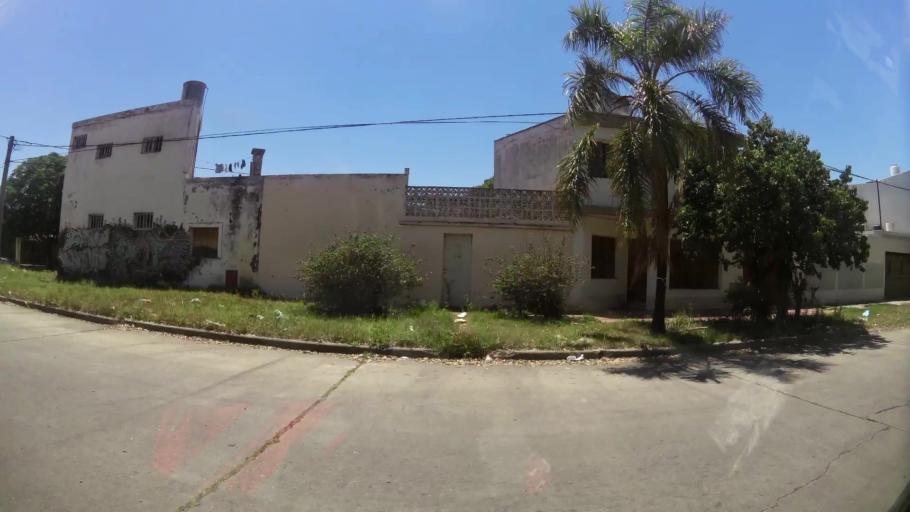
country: AR
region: Cordoba
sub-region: Departamento de Capital
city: Cordoba
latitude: -31.3999
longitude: -64.2112
